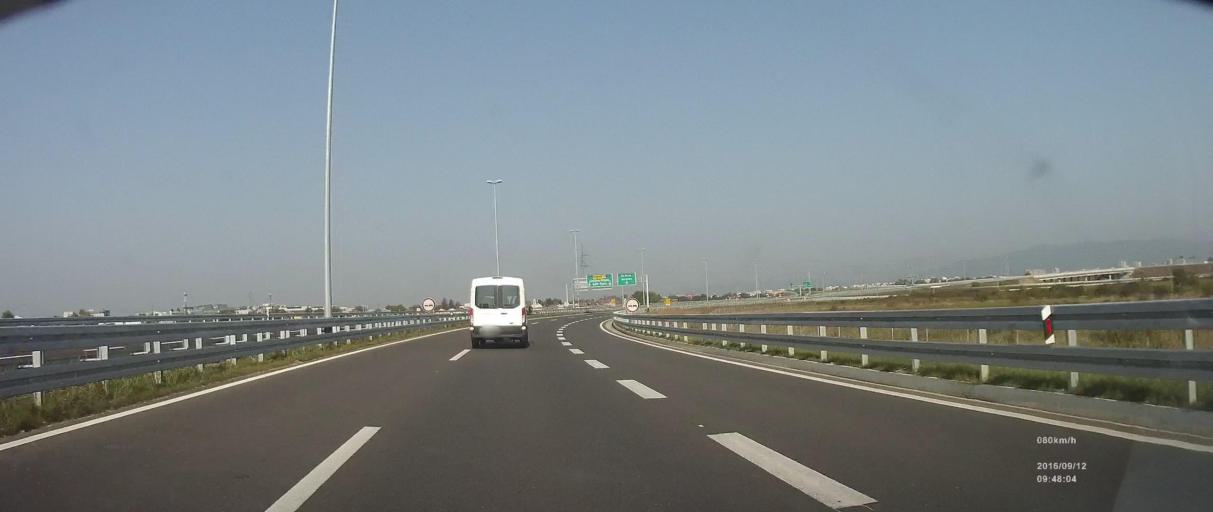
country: HR
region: Grad Zagreb
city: Odra
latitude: 45.7465
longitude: 16.0070
